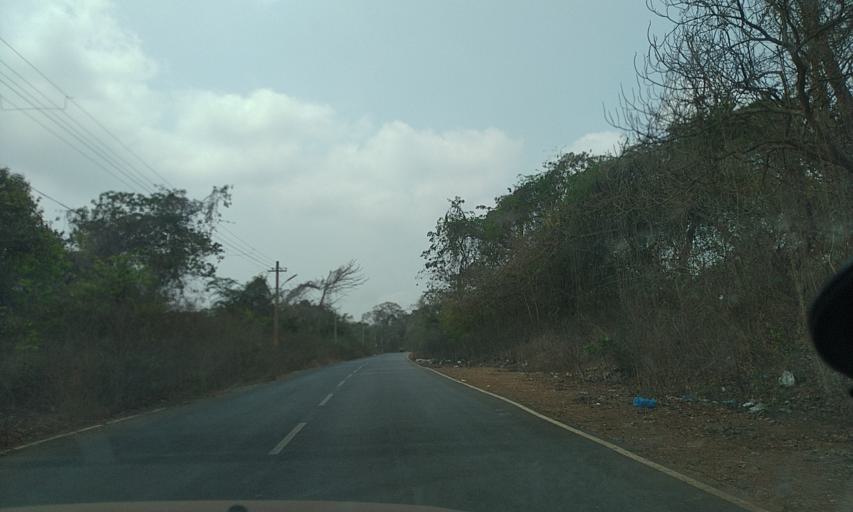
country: IN
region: Goa
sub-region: North Goa
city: Goa Velha
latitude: 15.4885
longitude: 73.9109
